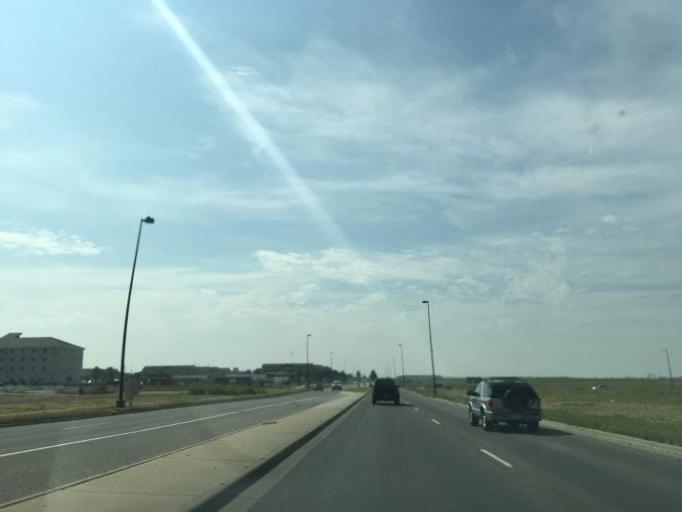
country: US
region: Colorado
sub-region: Adams County
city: Aurora
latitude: 39.8072
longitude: -104.7722
